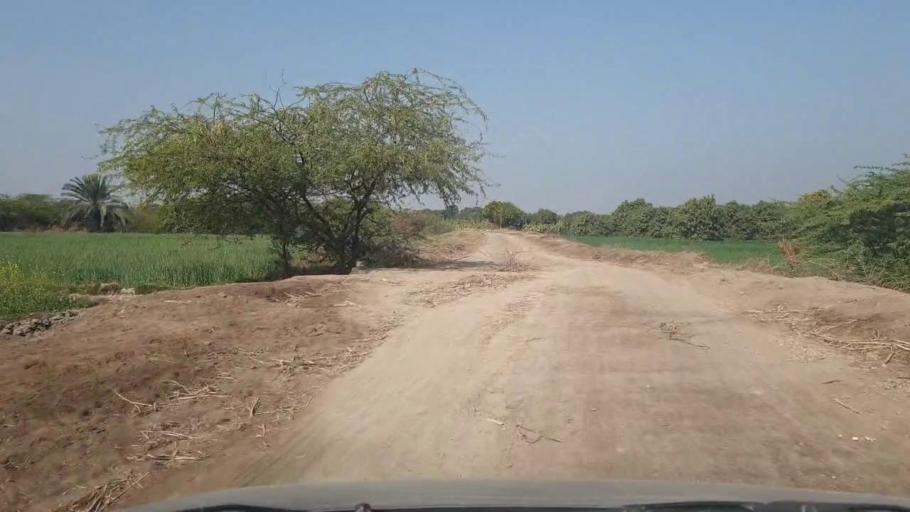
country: PK
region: Sindh
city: Mirwah Gorchani
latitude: 25.2473
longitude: 69.1063
